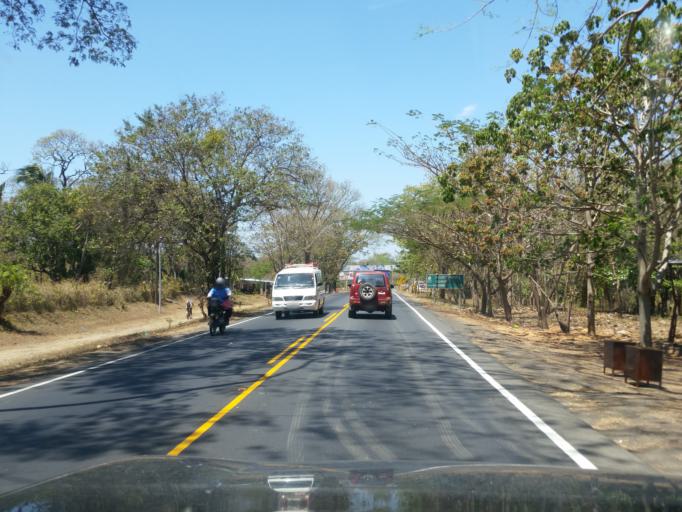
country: NI
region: Masaya
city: Masaya
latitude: 11.9526
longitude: -86.0918
